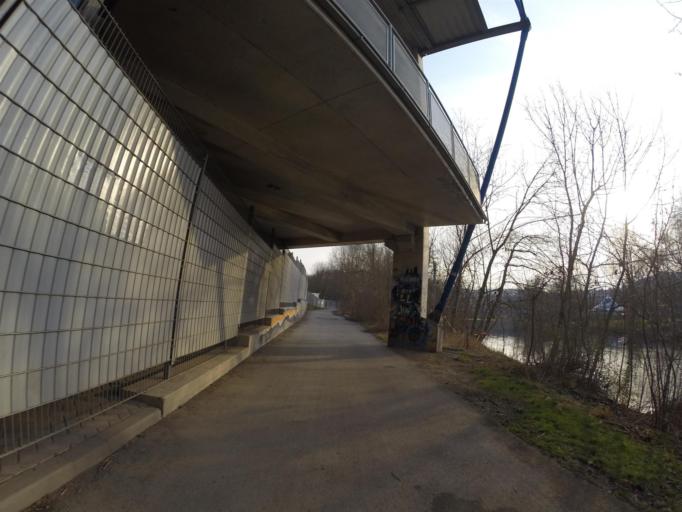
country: DE
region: Thuringia
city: Jena
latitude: 50.9164
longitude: 11.5819
